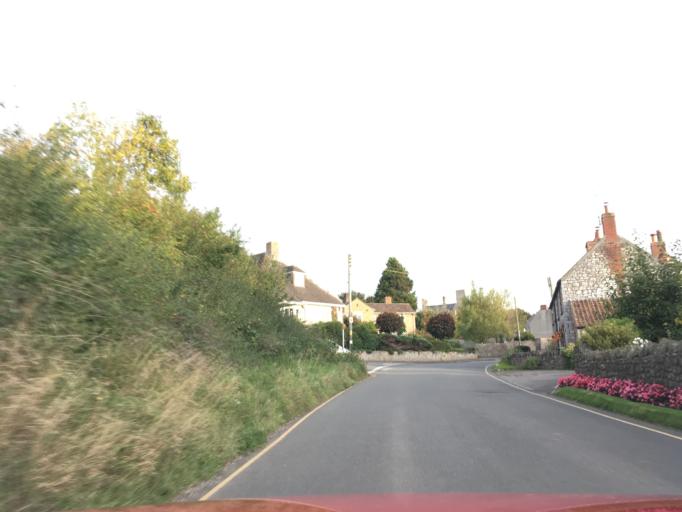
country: GB
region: England
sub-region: South Gloucestershire
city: Almondsbury
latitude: 51.5842
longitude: -2.5779
